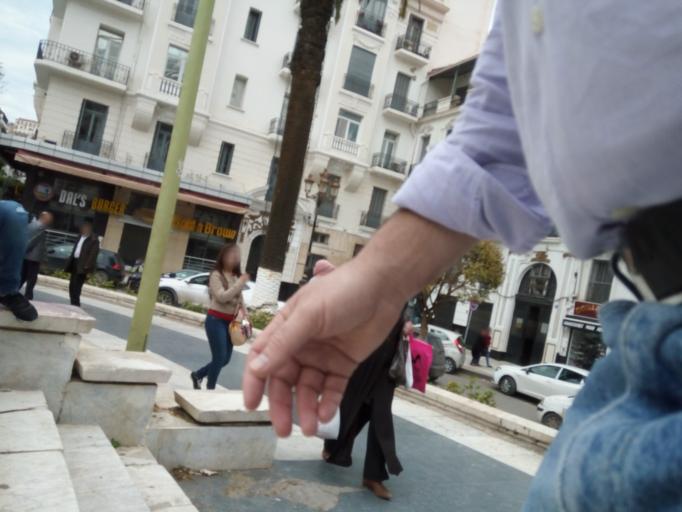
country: DZ
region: Alger
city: Algiers
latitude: 36.7762
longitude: 3.0584
